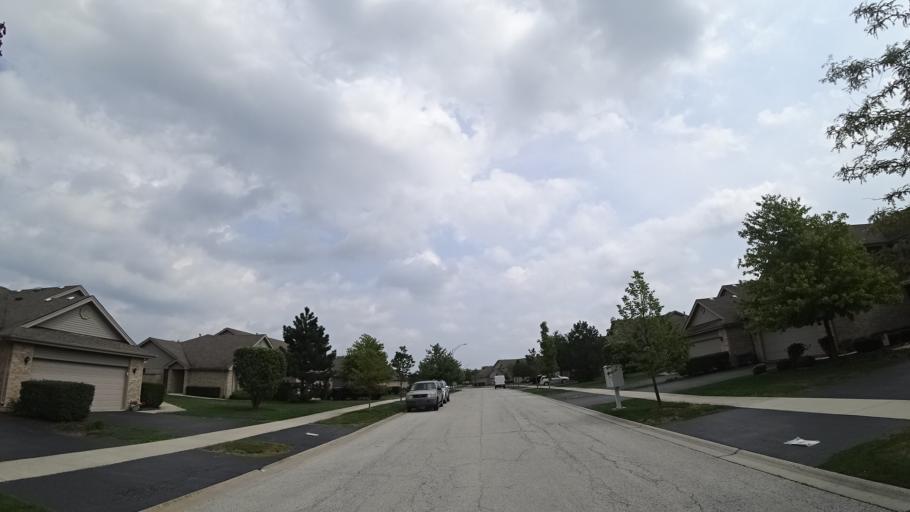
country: US
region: Illinois
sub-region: Will County
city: Goodings Grove
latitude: 41.6313
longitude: -87.9096
